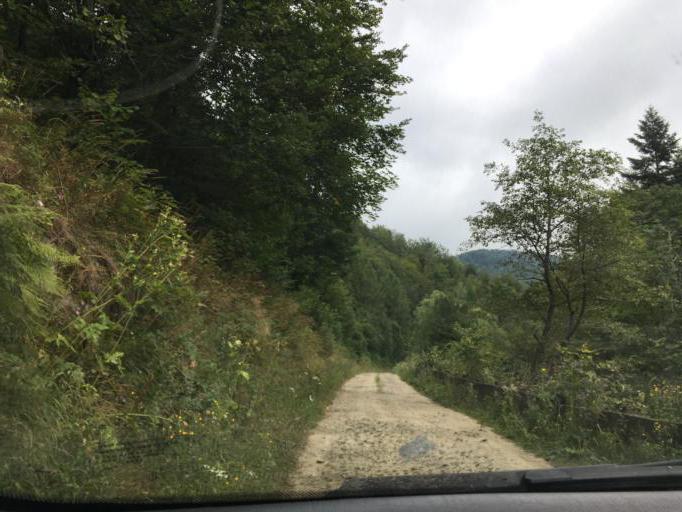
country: PL
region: Subcarpathian Voivodeship
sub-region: Powiat bieszczadzki
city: Lutowiska
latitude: 49.1756
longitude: 22.6138
